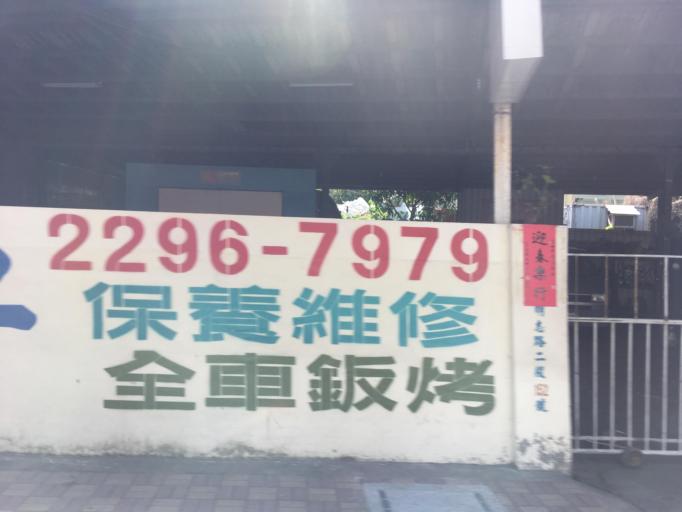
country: TW
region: Taipei
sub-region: Taipei
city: Banqiao
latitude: 25.0510
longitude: 121.4276
